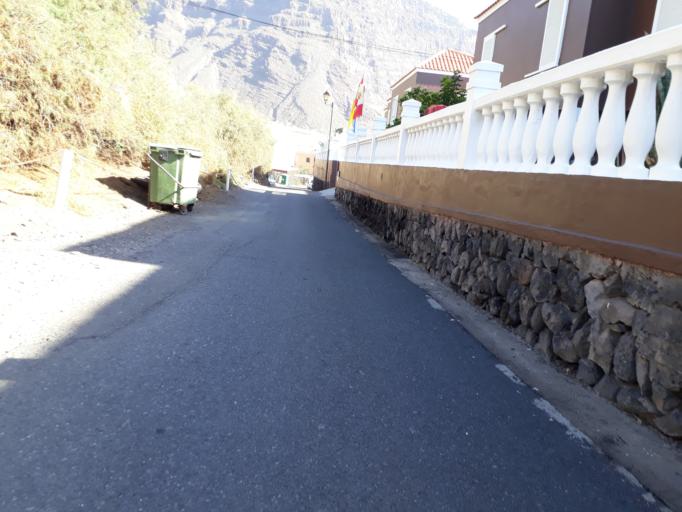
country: ES
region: Canary Islands
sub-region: Provincia de Santa Cruz de Tenerife
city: Alajero
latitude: 28.0966
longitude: -17.3448
